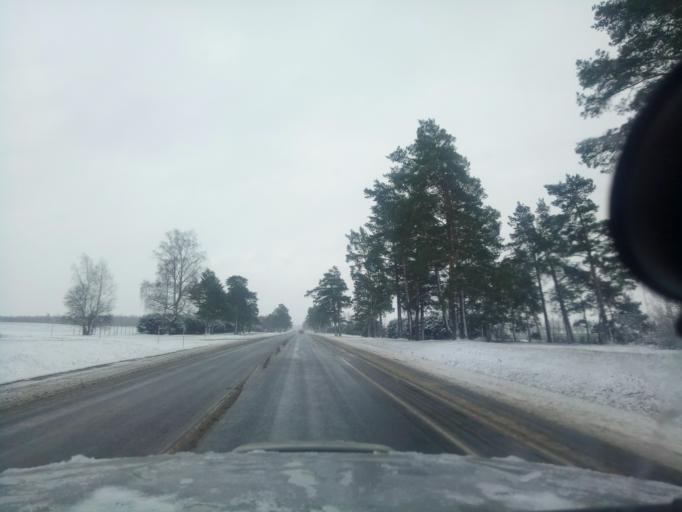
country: BY
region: Minsk
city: Nyasvizh
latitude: 53.2521
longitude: 26.6195
